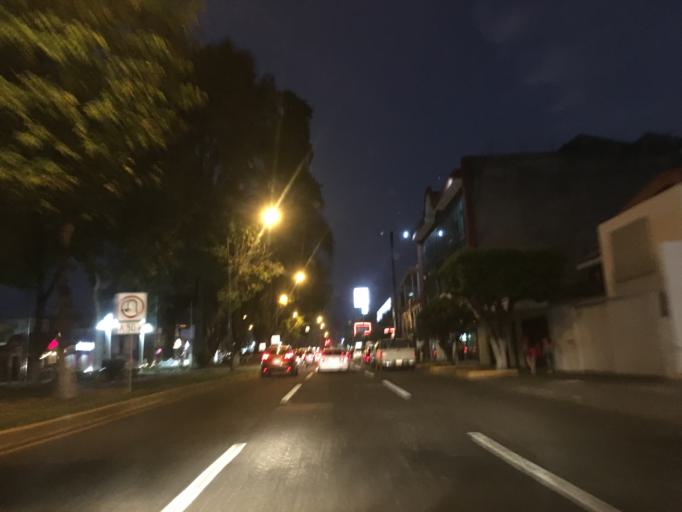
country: MX
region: Michoacan
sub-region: Uruapan
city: Uruapan
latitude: 19.3995
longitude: -102.0559
